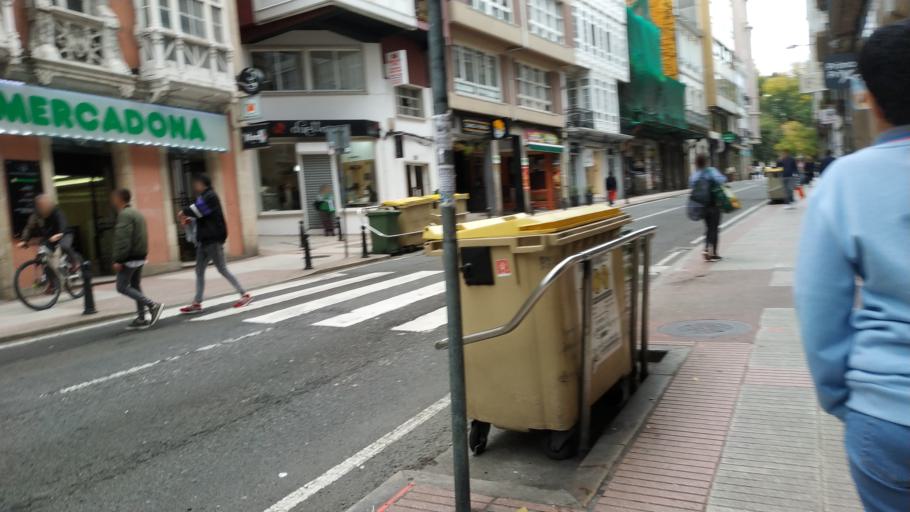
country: ES
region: Galicia
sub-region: Provincia da Coruna
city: A Coruna
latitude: 43.3728
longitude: -8.3986
